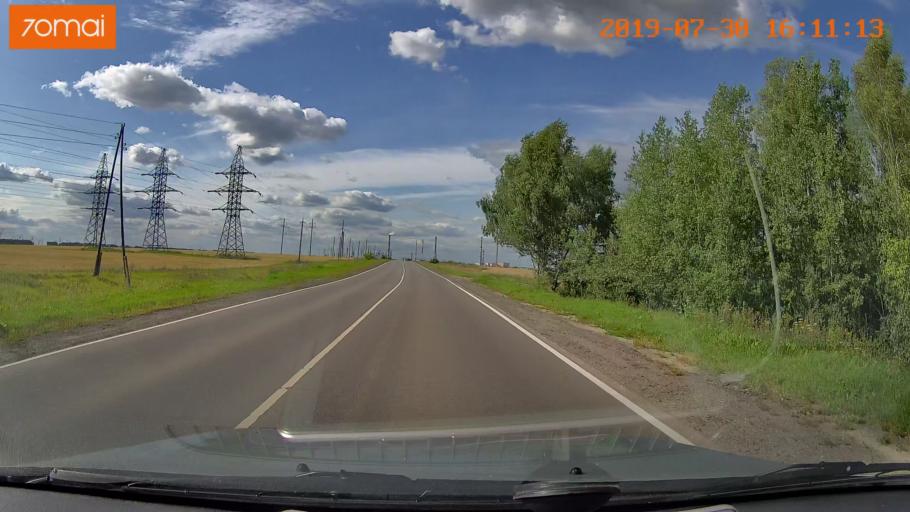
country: RU
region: Moskovskaya
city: Lopatinskiy
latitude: 55.2727
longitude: 38.7132
